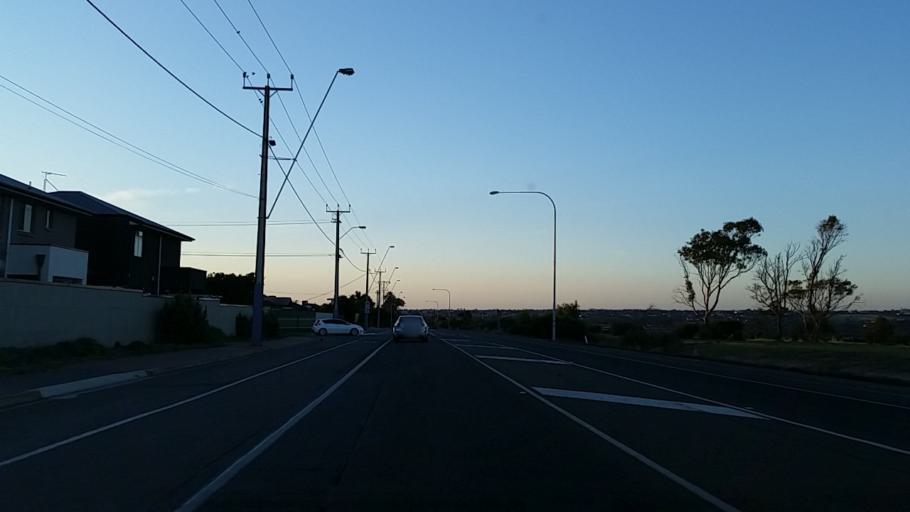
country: AU
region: South Australia
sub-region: Adelaide
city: Port Noarlunga
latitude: -35.1683
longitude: 138.4757
